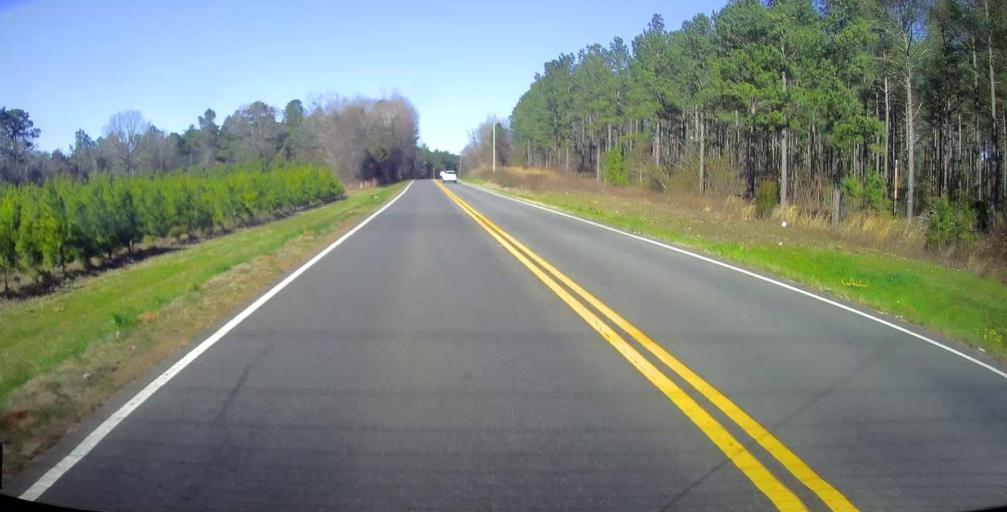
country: US
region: Georgia
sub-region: Macon County
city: Montezuma
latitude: 32.3476
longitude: -84.0191
